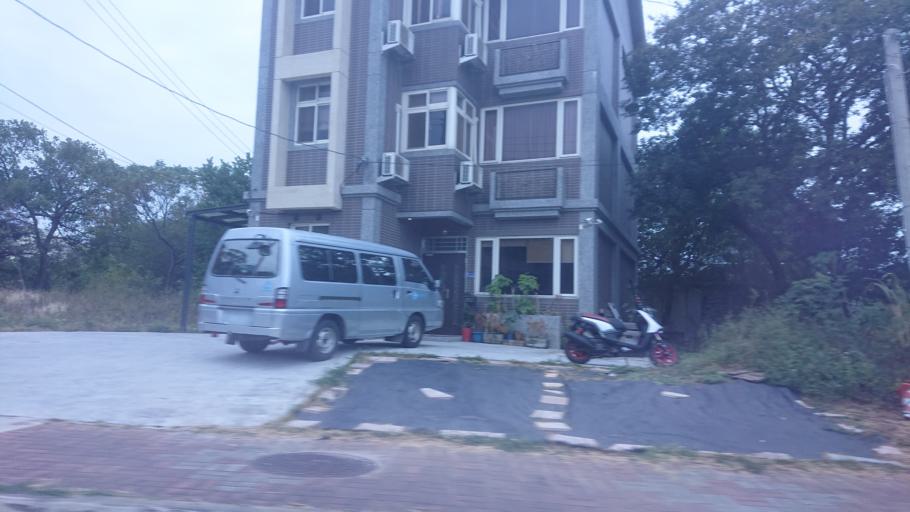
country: TW
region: Fukien
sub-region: Kinmen
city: Jincheng
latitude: 24.4372
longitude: 118.3119
